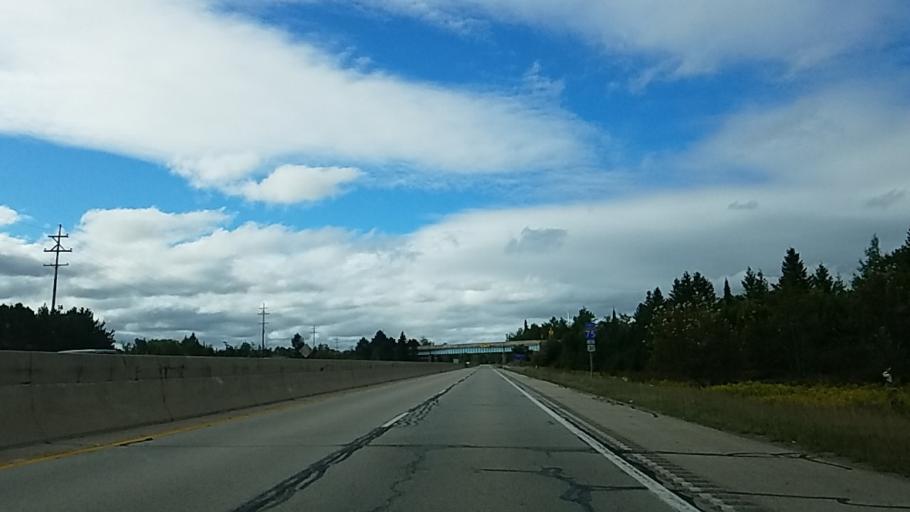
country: US
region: Michigan
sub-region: Mackinac County
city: Saint Ignace
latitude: 45.7745
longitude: -84.7343
